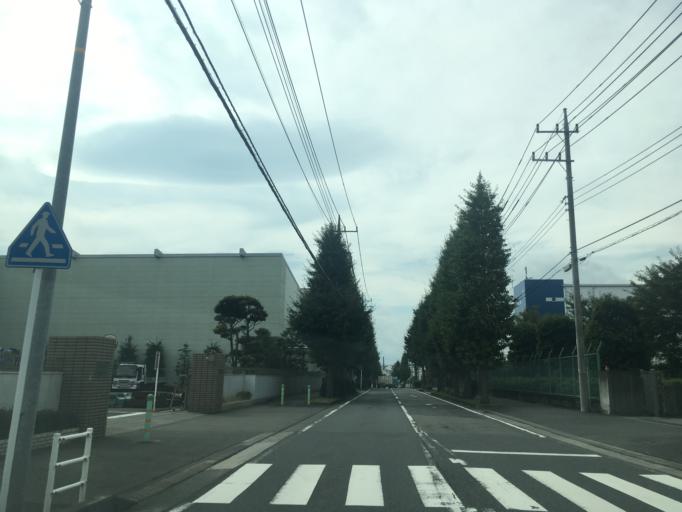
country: JP
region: Tokyo
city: Hachioji
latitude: 35.5882
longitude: 139.3507
